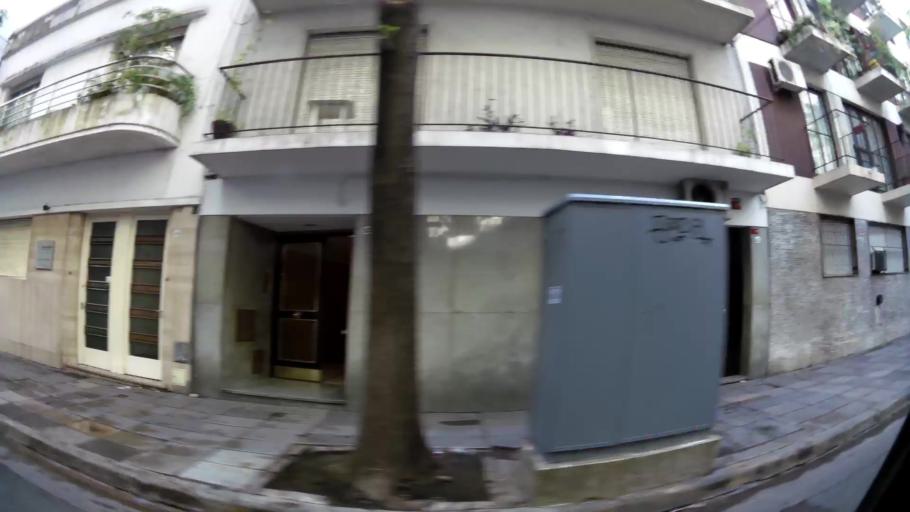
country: AR
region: Buenos Aires F.D.
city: Retiro
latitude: -34.5879
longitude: -58.3996
